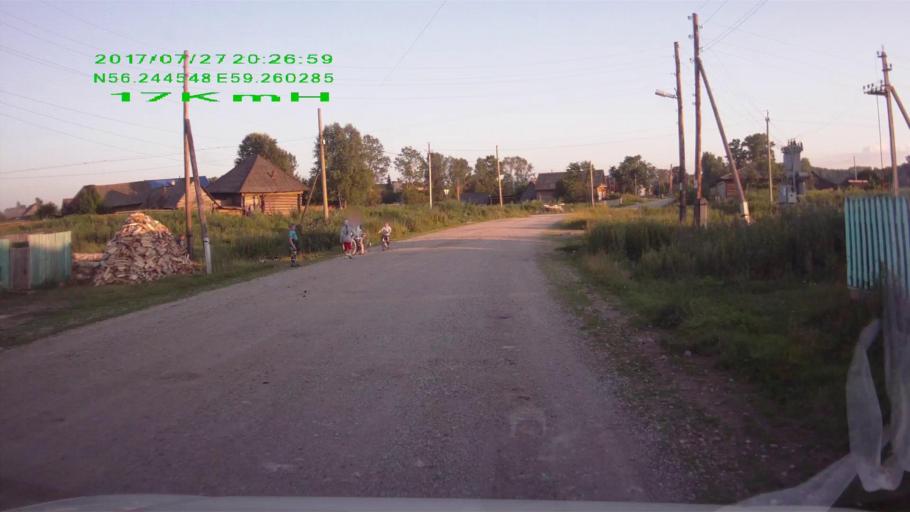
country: RU
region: Sverdlovsk
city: Mikhaylovsk
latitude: 56.2443
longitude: 59.2602
